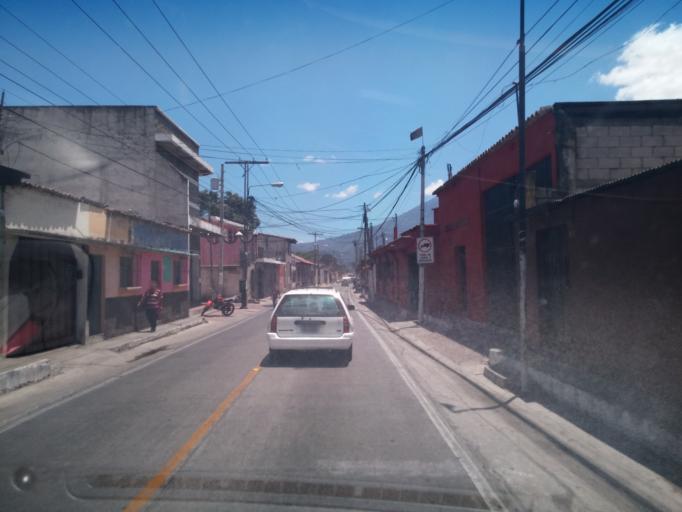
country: GT
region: Sacatepequez
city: Jocotenango
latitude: 14.5774
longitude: -90.7426
